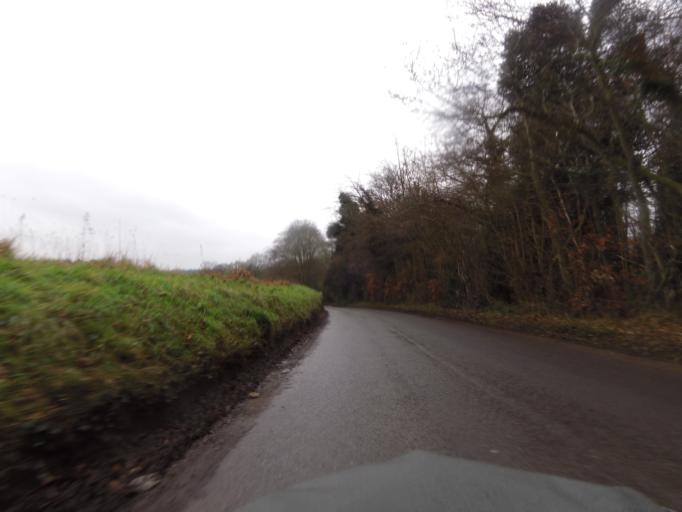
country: GB
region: England
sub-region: Norfolk
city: Briston
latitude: 52.8773
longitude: 1.0769
